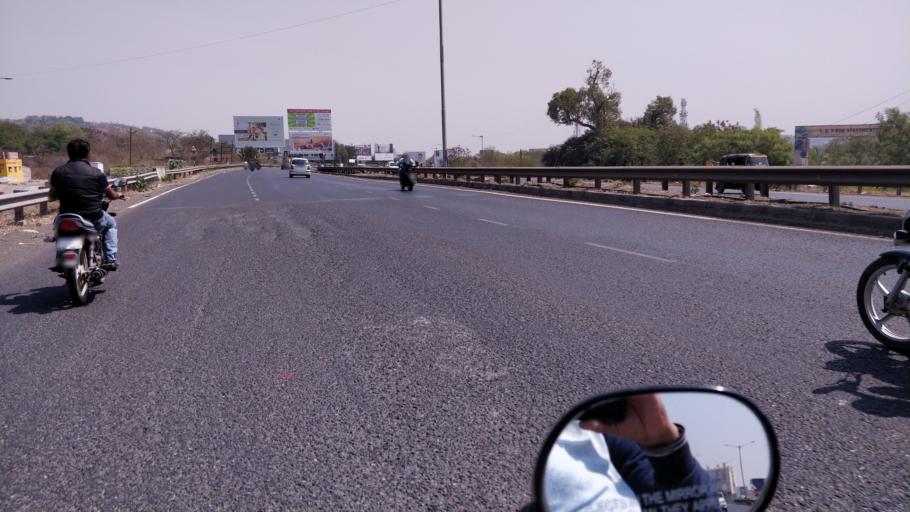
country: IN
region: Maharashtra
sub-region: Pune Division
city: Shivaji Nagar
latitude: 18.5243
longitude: 73.7714
